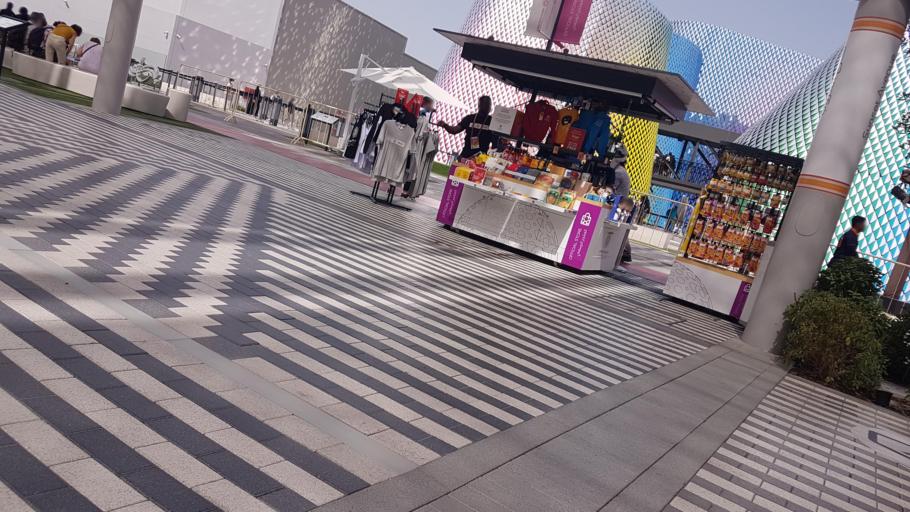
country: AE
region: Dubai
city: Dubai
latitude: 24.9654
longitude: 55.1517
